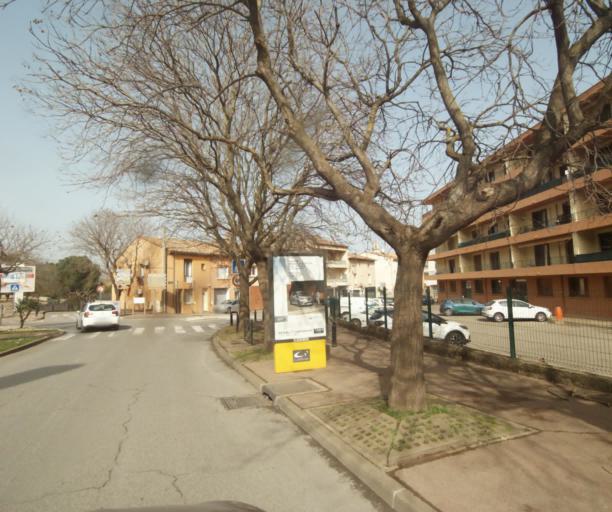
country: FR
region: Provence-Alpes-Cote d'Azur
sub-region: Departement des Bouches-du-Rhone
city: Gardanne
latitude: 43.4520
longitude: 5.4687
